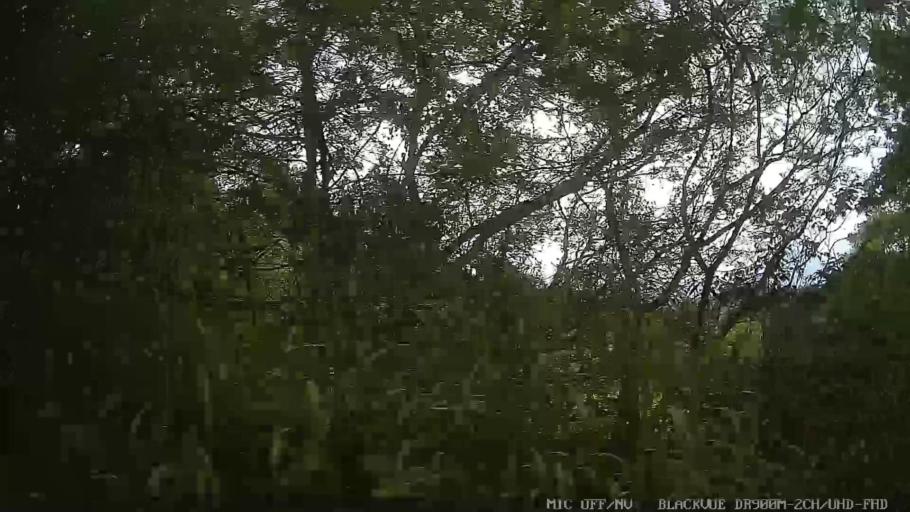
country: BR
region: Sao Paulo
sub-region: Mogi das Cruzes
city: Mogi das Cruzes
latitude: -23.5193
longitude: -46.2278
